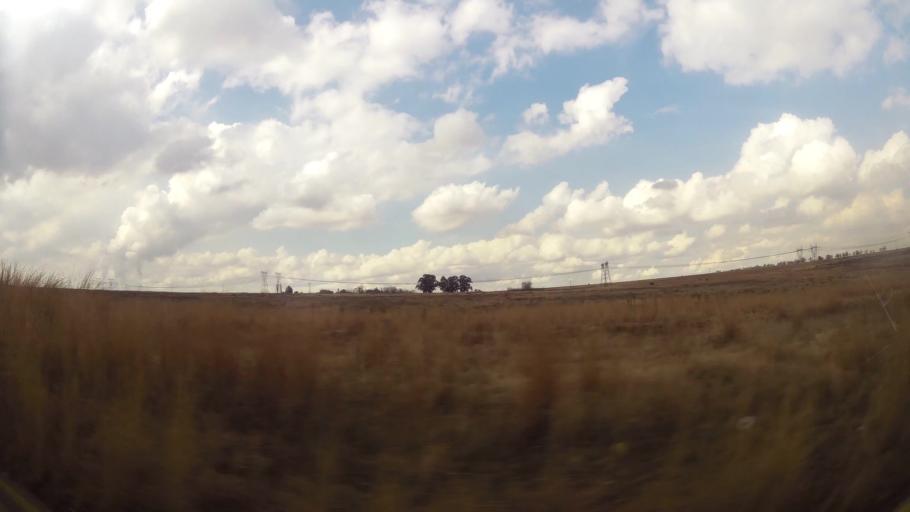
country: ZA
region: Orange Free State
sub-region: Fezile Dabi District Municipality
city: Sasolburg
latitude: -26.7838
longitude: 27.9179
